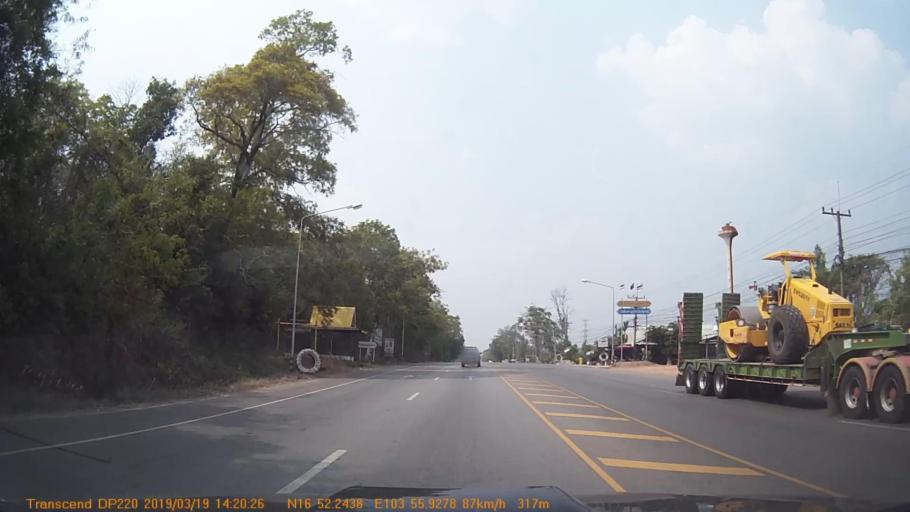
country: TH
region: Sakon Nakhon
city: Phu Phan
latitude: 16.8714
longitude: 103.9320
